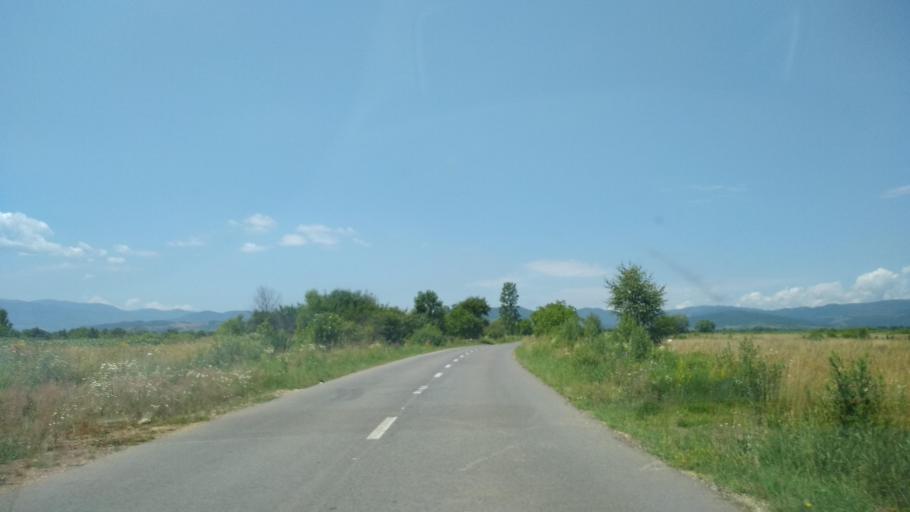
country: RO
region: Hunedoara
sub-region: Comuna Totesti
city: Totesti
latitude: 45.5729
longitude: 22.8775
